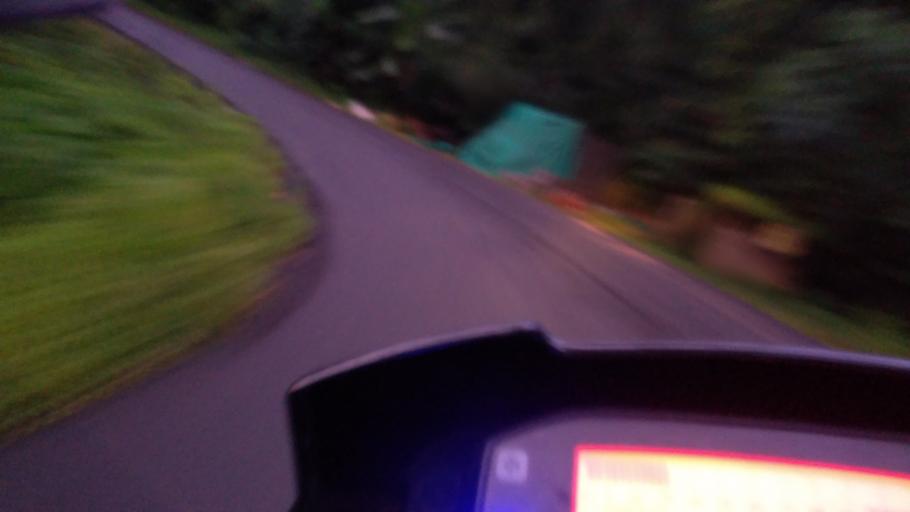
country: IN
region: Kerala
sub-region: Idukki
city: Munnar
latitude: 9.9629
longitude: 77.0705
